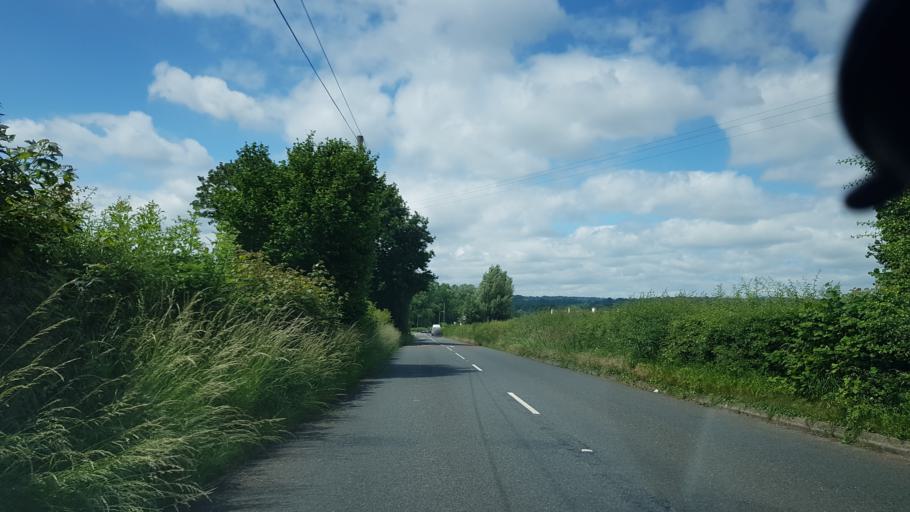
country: GB
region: Wales
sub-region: Monmouthshire
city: Llangwm
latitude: 51.7113
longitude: -2.8517
